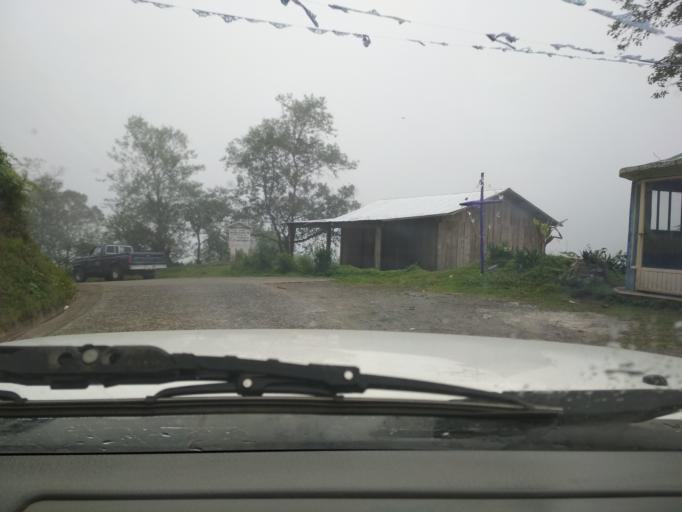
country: MX
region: Veracruz
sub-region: La Perla
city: Barrio de San Miguel
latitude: 18.9549
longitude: -97.1289
